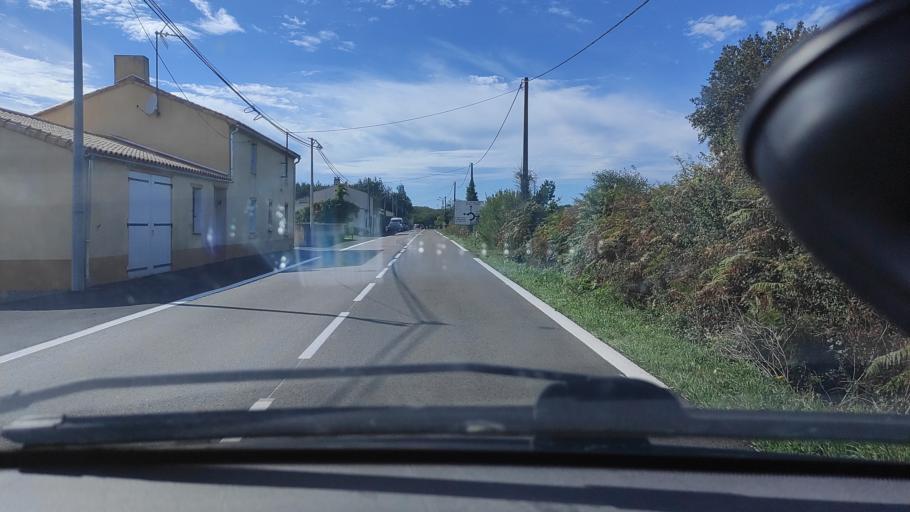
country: FR
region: Pays de la Loire
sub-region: Departement de la Vendee
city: La Boissiere-des-Landes
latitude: 46.5587
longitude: -1.4462
